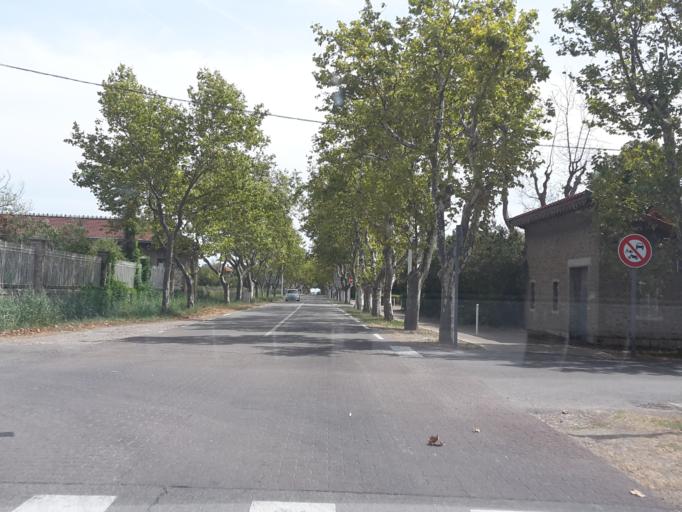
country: FR
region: Provence-Alpes-Cote d'Azur
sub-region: Departement des Bouches-du-Rhone
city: Port-Saint-Louis-du-Rhone
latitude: 43.4181
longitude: 4.7353
